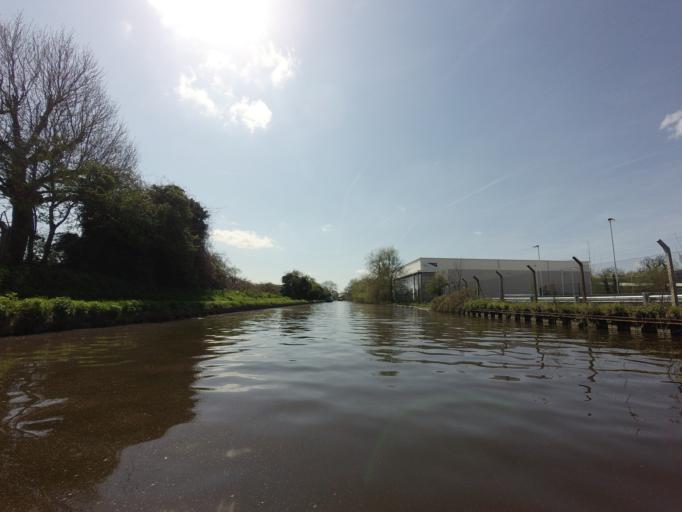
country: GB
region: England
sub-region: Greater London
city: Southall
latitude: 51.5106
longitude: -0.3916
